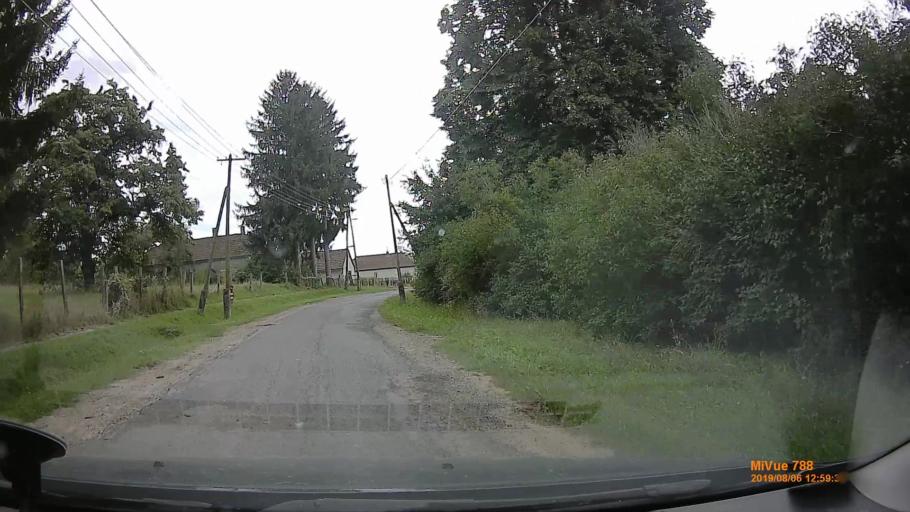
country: HU
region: Zala
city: Pacsa
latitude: 46.6233
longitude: 17.0468
